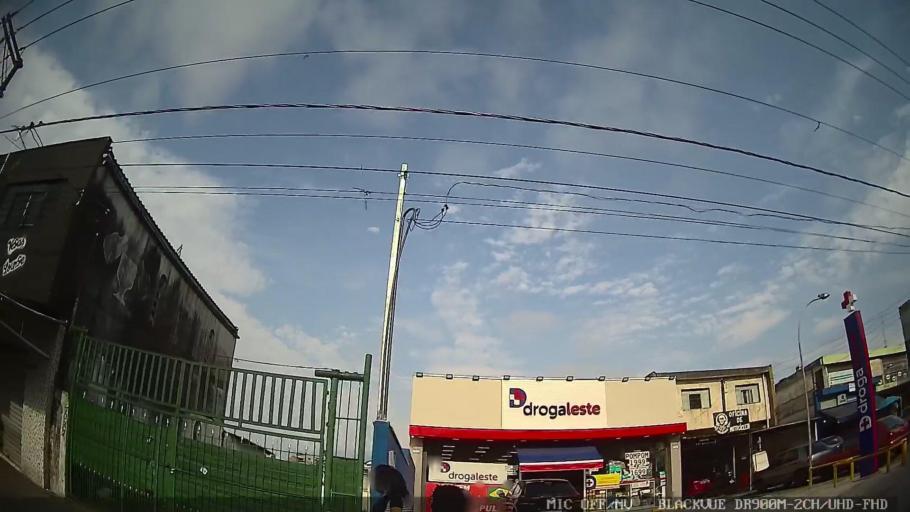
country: BR
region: Sao Paulo
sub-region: Ferraz De Vasconcelos
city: Ferraz de Vasconcelos
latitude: -23.5212
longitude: -46.3997
